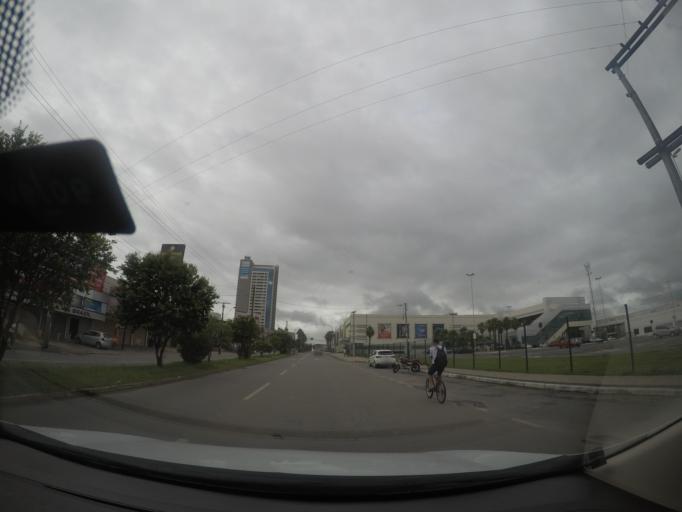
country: BR
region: Goias
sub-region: Goiania
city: Goiania
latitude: -16.7409
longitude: -49.2745
